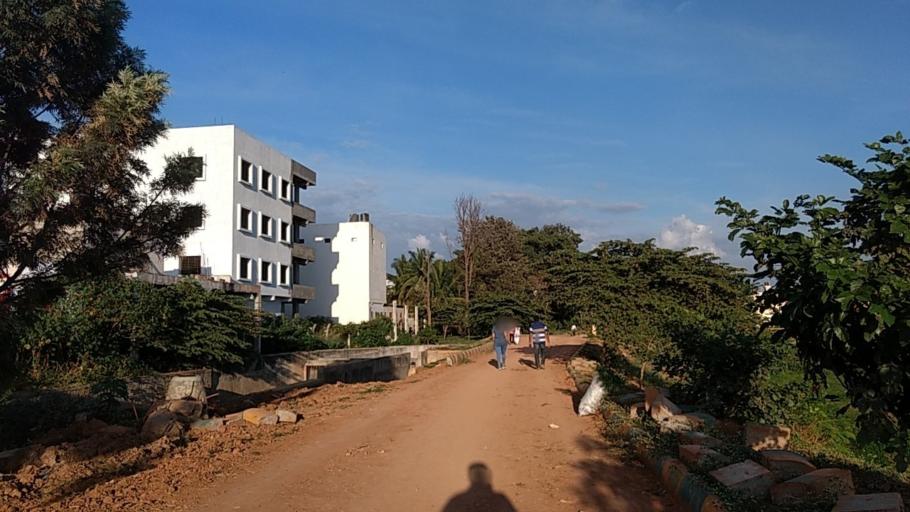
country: IN
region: Karnataka
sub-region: Bangalore Urban
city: Yelahanka
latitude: 13.0688
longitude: 77.5621
